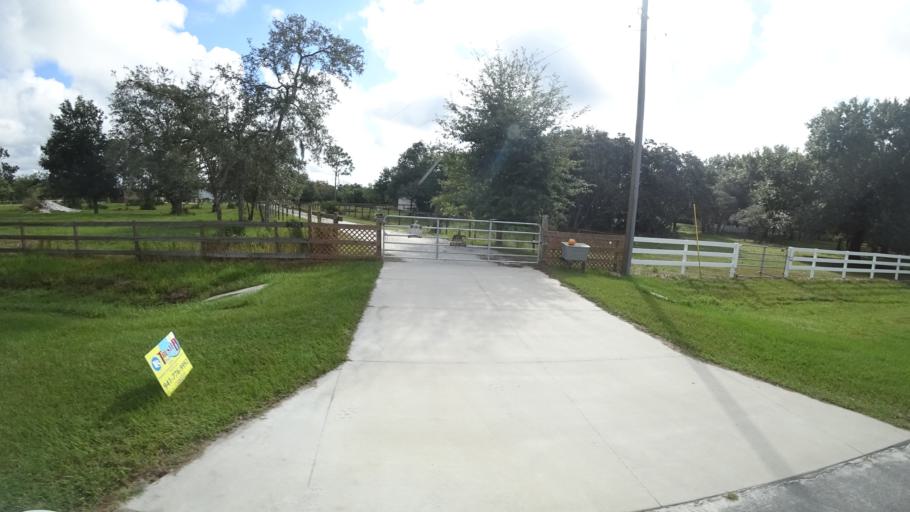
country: US
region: Florida
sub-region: Sarasota County
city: Lake Sarasota
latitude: 27.3645
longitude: -82.2506
